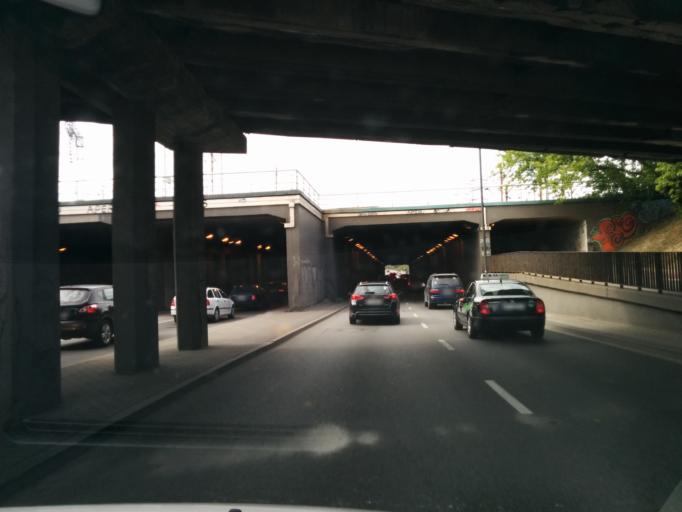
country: PL
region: Masovian Voivodeship
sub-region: Warszawa
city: Ochota
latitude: 52.2180
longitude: 20.9602
